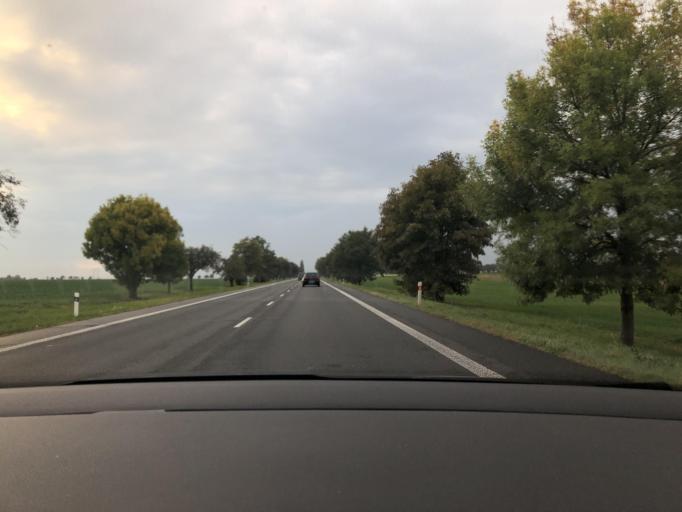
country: CZ
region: Central Bohemia
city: Velim
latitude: 50.0414
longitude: 15.0983
